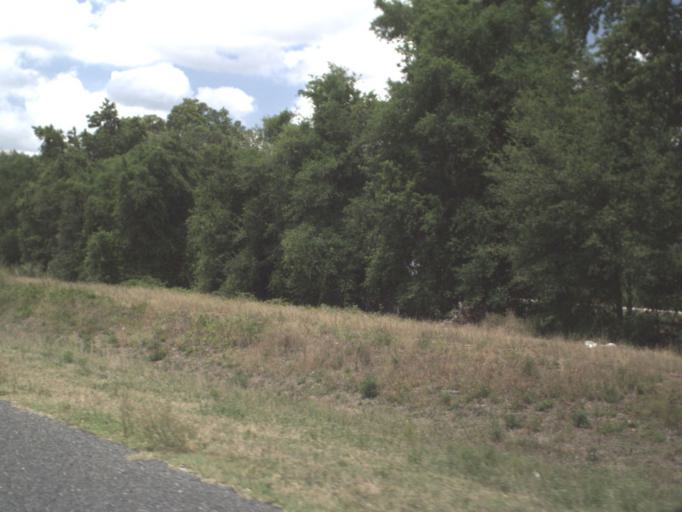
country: US
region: Florida
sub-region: Sumter County
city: Wildwood
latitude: 28.8244
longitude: -81.9760
